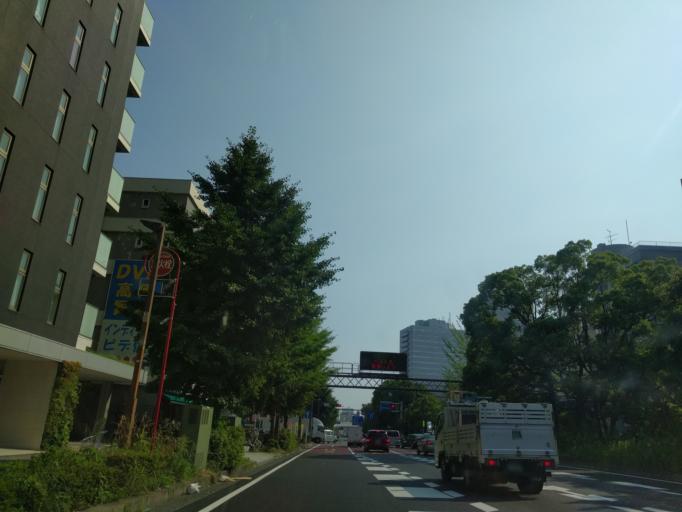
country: JP
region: Kanagawa
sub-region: Kawasaki-shi
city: Kawasaki
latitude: 35.5323
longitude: 139.7067
